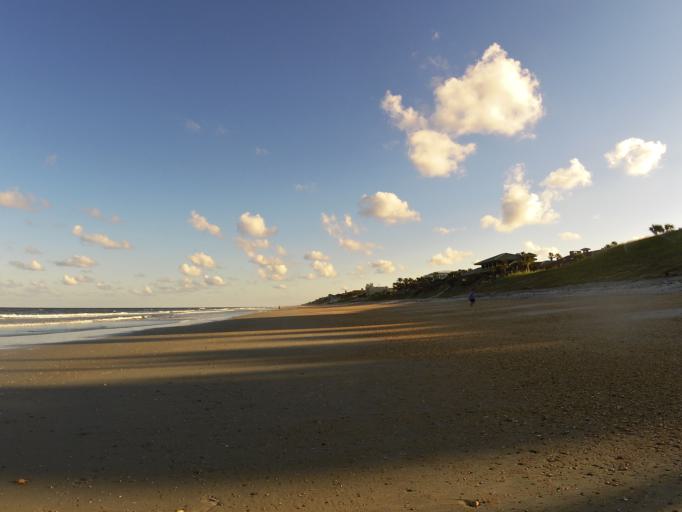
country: US
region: Florida
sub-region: Saint Johns County
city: Sawgrass
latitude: 30.1771
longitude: -81.3595
